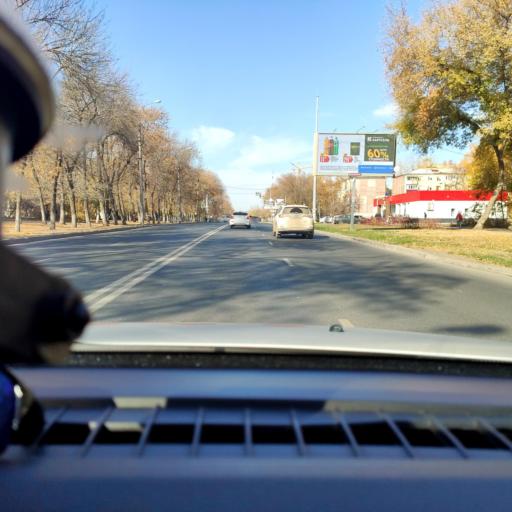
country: RU
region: Samara
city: Samara
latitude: 53.2174
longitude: 50.2081
